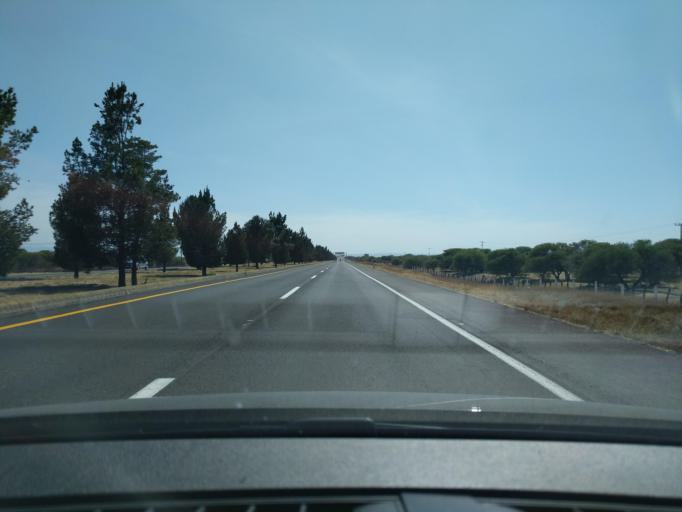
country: MX
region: Durango
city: Victoria de Durango
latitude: 24.1207
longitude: -104.5438
